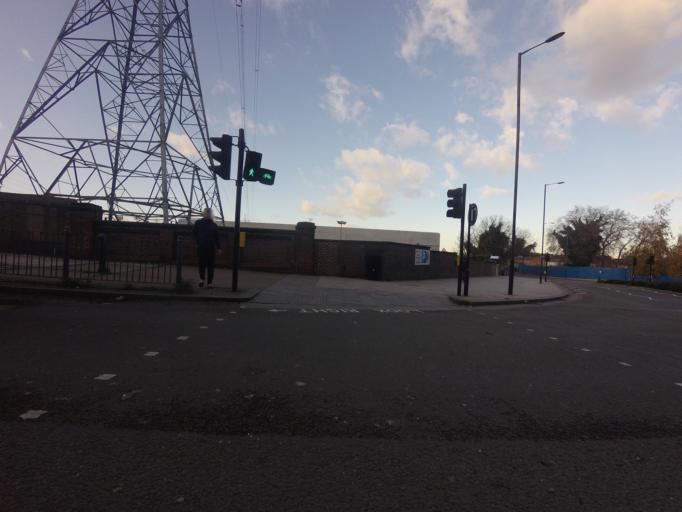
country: GB
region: England
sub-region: Greater London
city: Poplar
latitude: 51.5156
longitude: 0.0074
